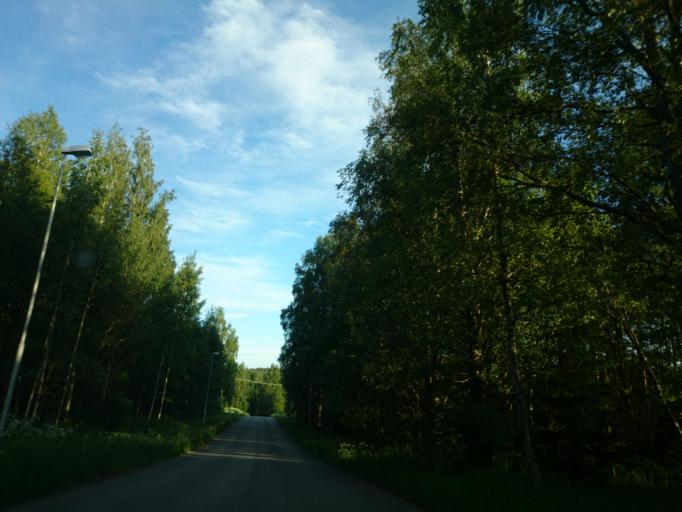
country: SE
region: Vaesternorrland
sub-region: Sundsvalls Kommun
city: Stockvik
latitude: 62.3365
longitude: 17.3605
